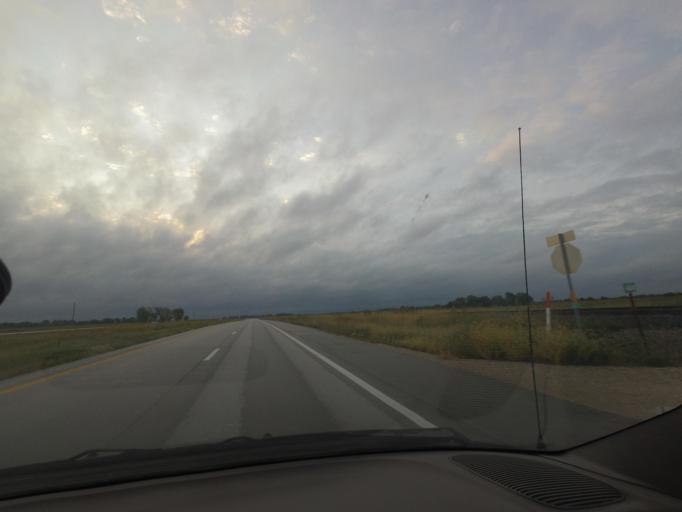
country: US
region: Missouri
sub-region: Shelby County
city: Shelbina
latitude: 39.6781
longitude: -91.9735
